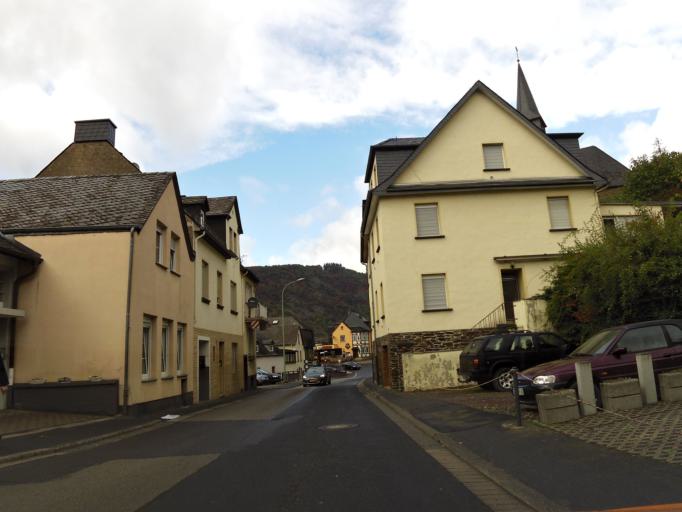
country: DE
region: Rheinland-Pfalz
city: Cochem
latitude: 50.1464
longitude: 7.1704
